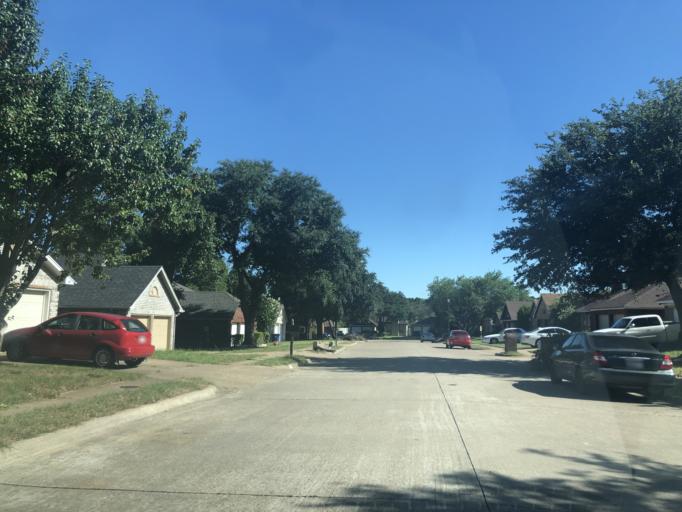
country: US
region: Texas
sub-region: Dallas County
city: Duncanville
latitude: 32.6637
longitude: -96.9328
